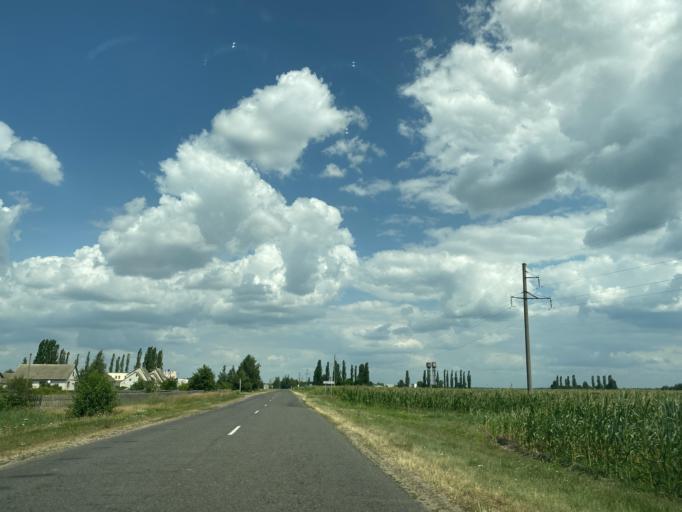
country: BY
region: Brest
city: Ivanava
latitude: 52.3426
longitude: 25.6259
